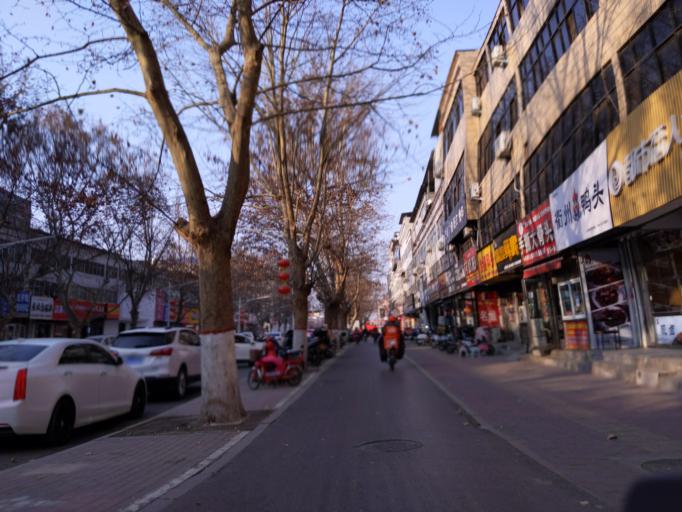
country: CN
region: Henan Sheng
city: Puyang
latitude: 35.7706
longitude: 115.0326
